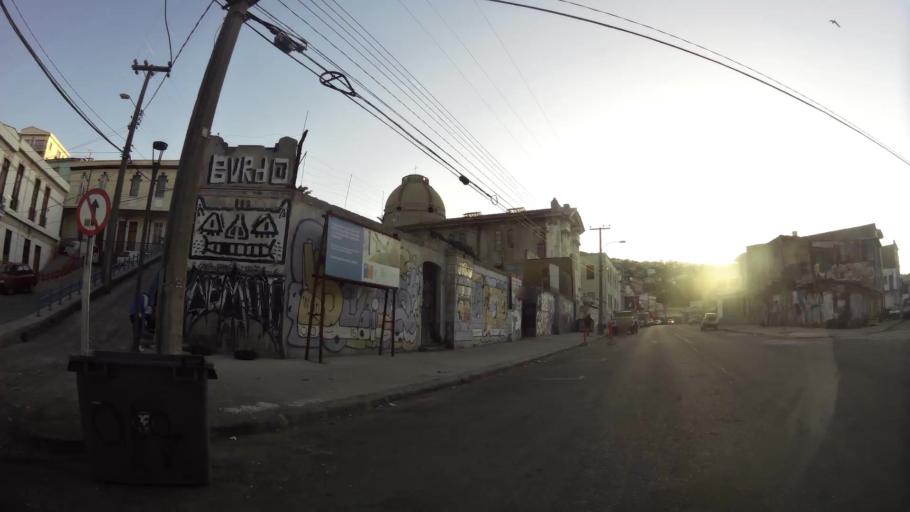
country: CL
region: Valparaiso
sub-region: Provincia de Valparaiso
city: Valparaiso
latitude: -33.0517
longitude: -71.6061
